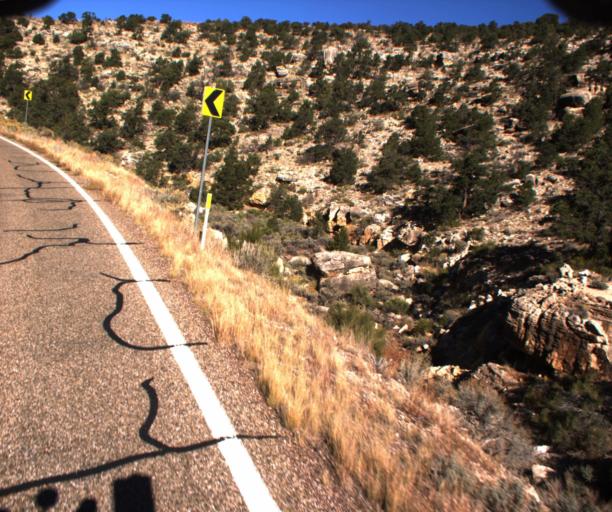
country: US
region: Arizona
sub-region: Coconino County
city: Fredonia
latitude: 36.7255
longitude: -112.0824
